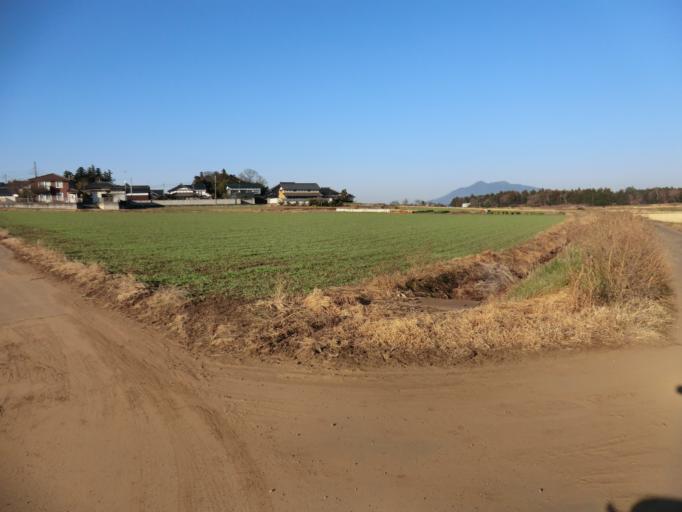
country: JP
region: Ibaraki
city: Ishige
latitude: 36.0994
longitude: 140.0315
